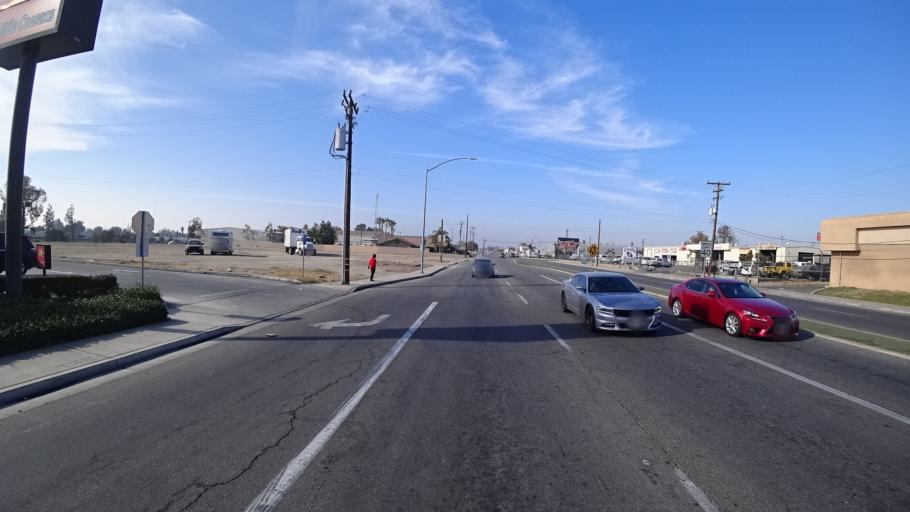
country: US
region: California
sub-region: Kern County
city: Bakersfield
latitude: 35.3538
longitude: -119.0036
